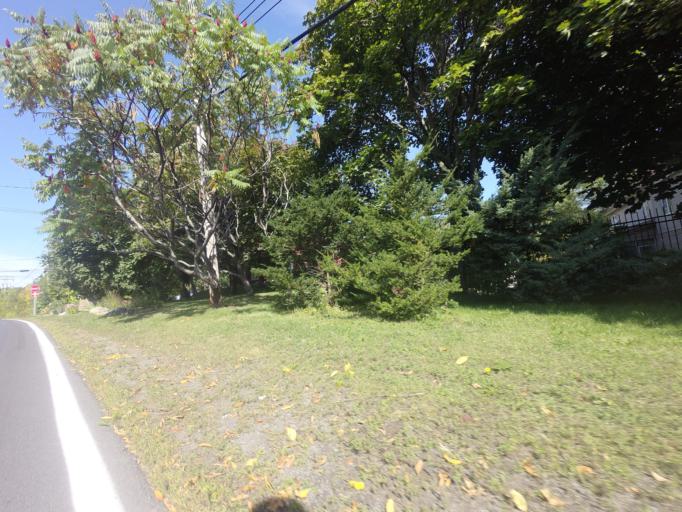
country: CA
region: Quebec
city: Dollard-Des Ormeaux
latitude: 45.5103
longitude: -73.8583
